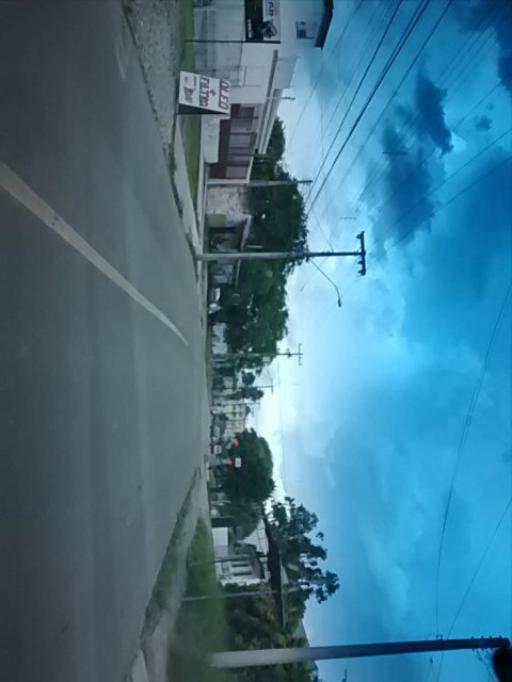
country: BR
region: Rio Grande do Sul
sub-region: Santa Maria
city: Santa Maria
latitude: -29.6899
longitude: -53.8341
